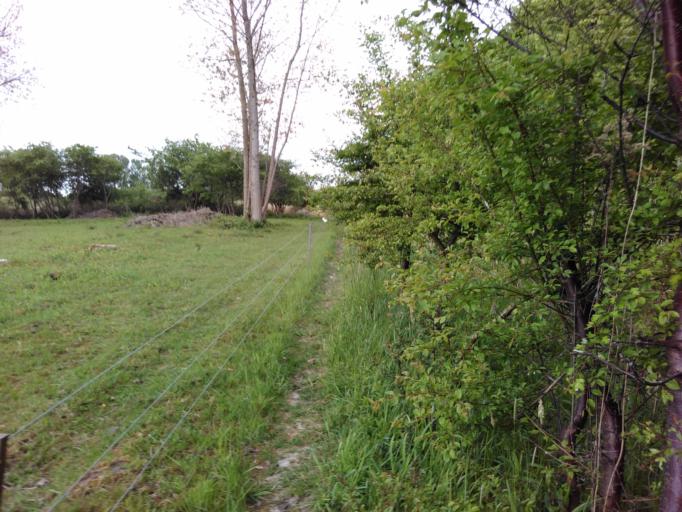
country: DK
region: Capital Region
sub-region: Kobenhavn
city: Christianshavn
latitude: 55.6505
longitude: 12.5804
